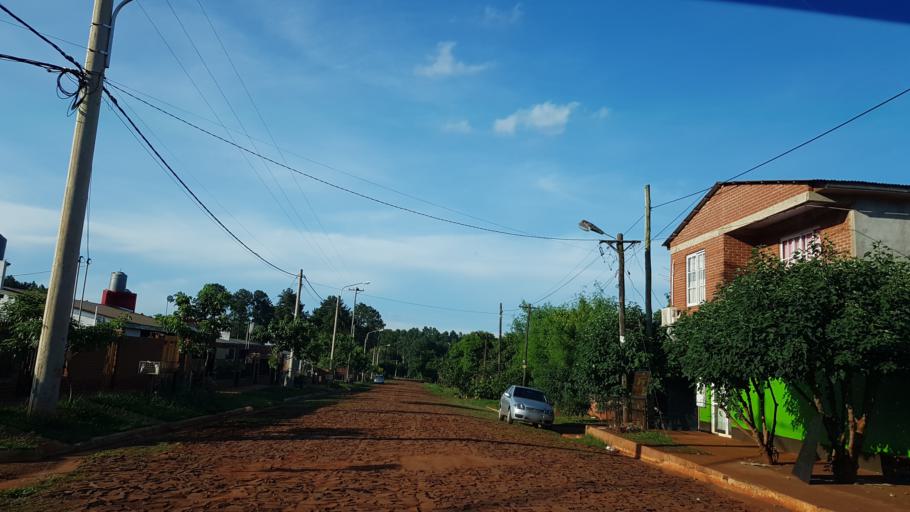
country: AR
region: Misiones
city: Puerto Libertad
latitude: -25.9189
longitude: -54.5895
